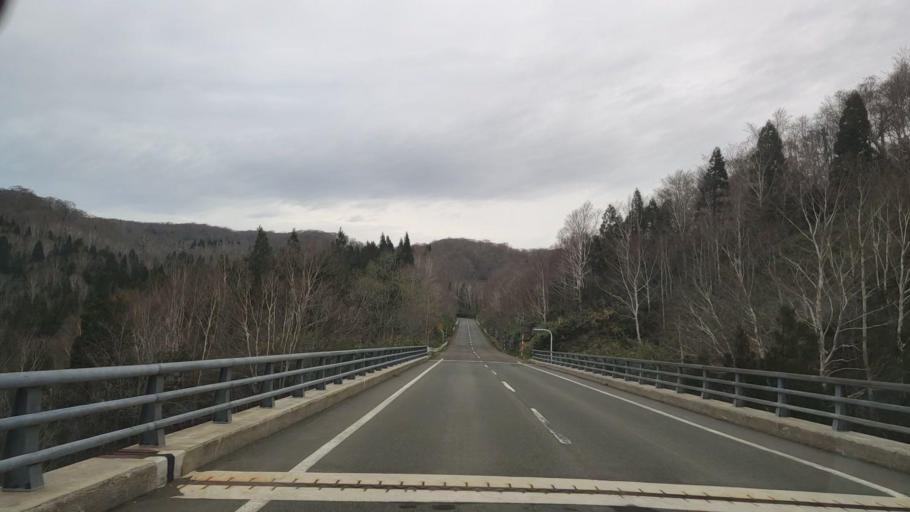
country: JP
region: Akita
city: Hanawa
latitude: 40.4135
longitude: 140.8462
